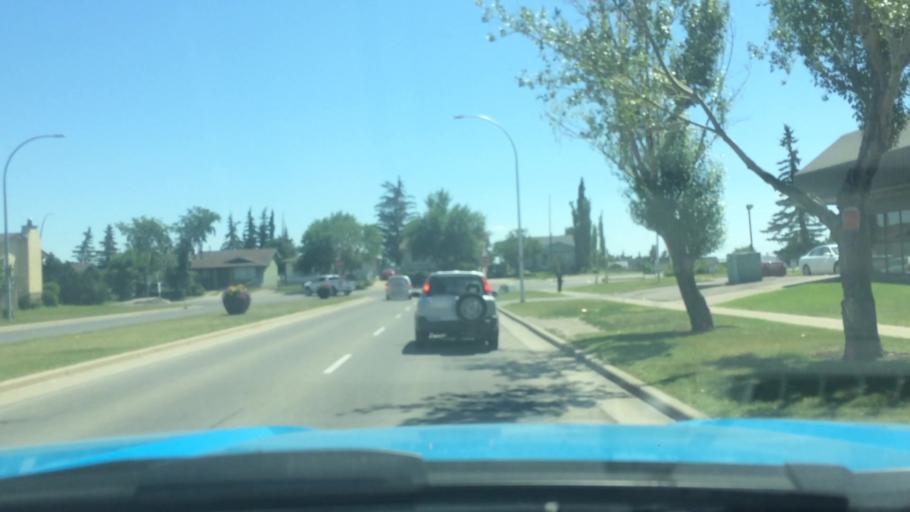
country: CA
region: Alberta
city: Calgary
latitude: 51.0477
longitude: -113.9893
